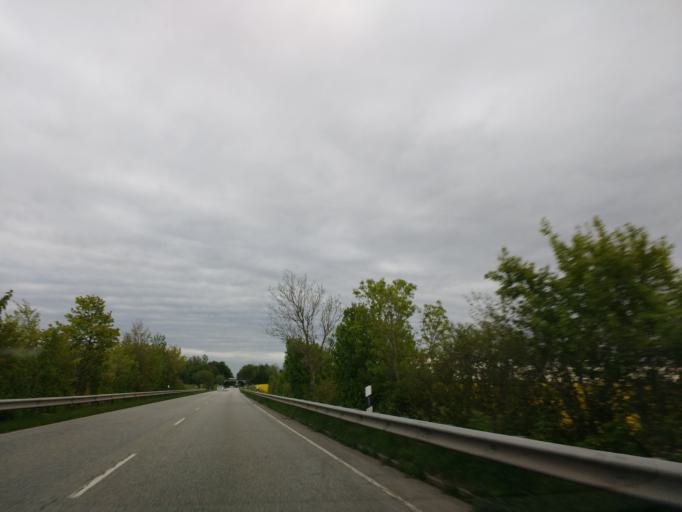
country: DE
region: Schleswig-Holstein
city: Brodersby
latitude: 54.6419
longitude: 9.9606
